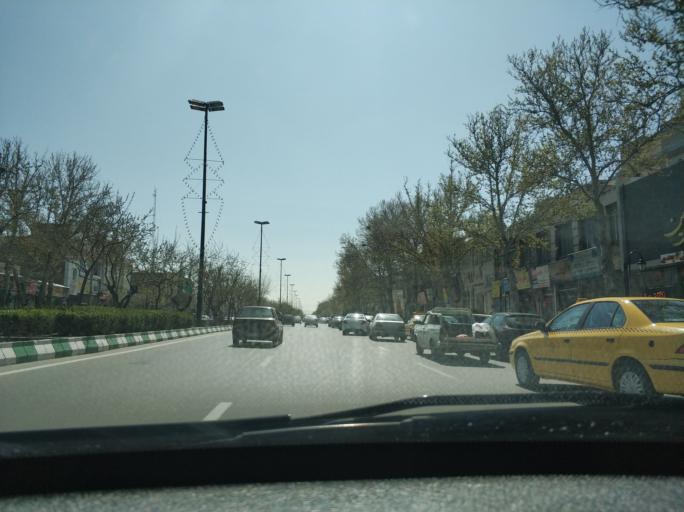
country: IR
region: Razavi Khorasan
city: Mashhad
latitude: 36.2669
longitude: 59.5998
